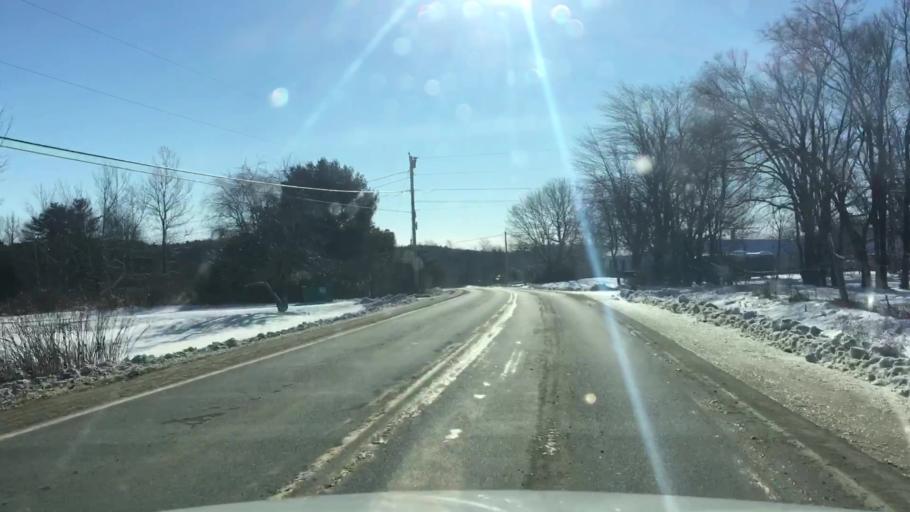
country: US
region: Maine
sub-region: Kennebec County
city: Readfield
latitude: 44.3622
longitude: -69.9899
